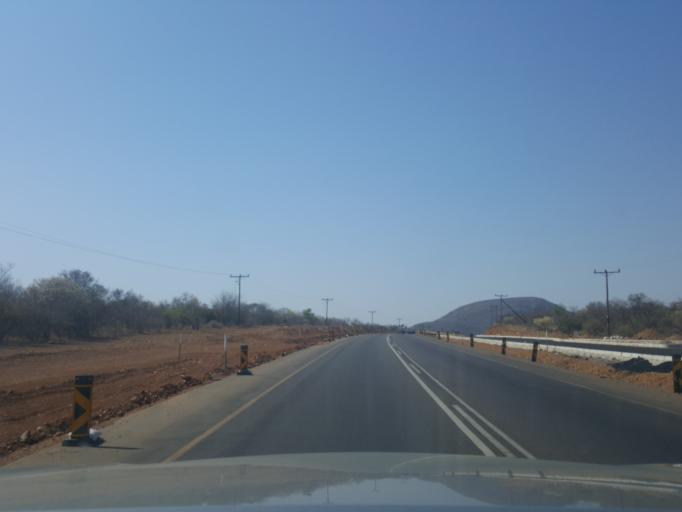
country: BW
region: Kweneng
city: Gabane
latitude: -24.7501
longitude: 25.8288
